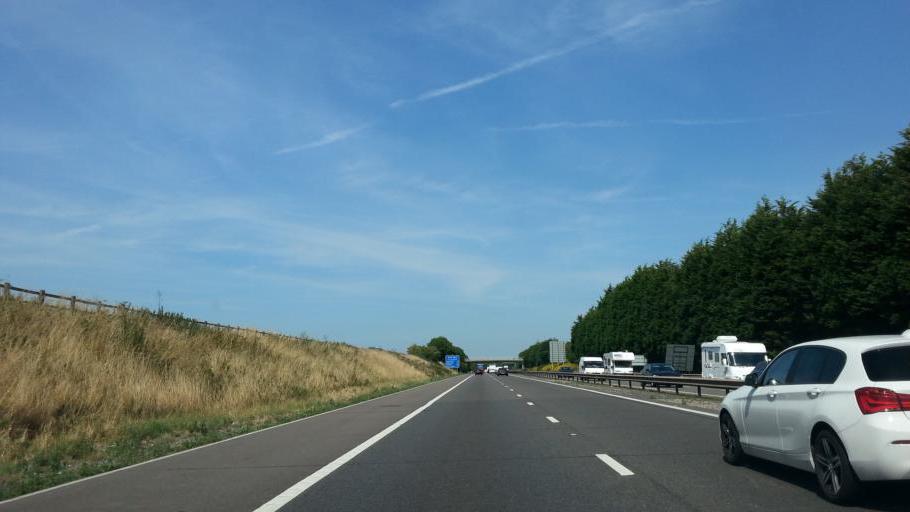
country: GB
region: England
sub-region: Warwickshire
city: Curdworth
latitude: 52.5510
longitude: -1.7148
